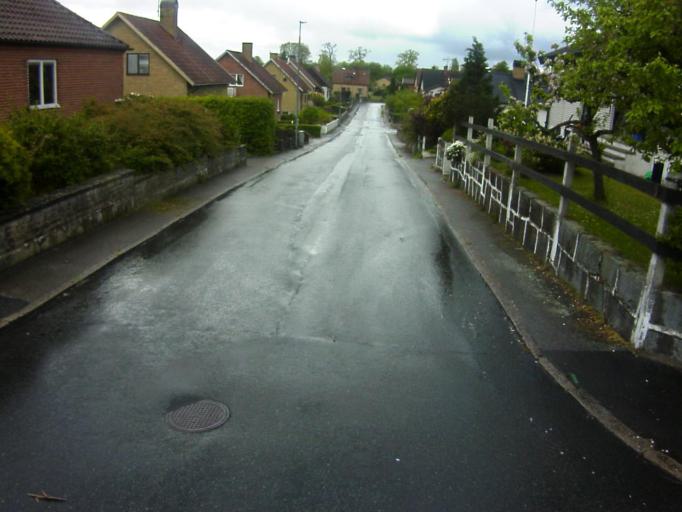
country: SE
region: Blekinge
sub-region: Solvesborgs Kommun
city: Soelvesborg
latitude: 56.0567
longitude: 14.5794
